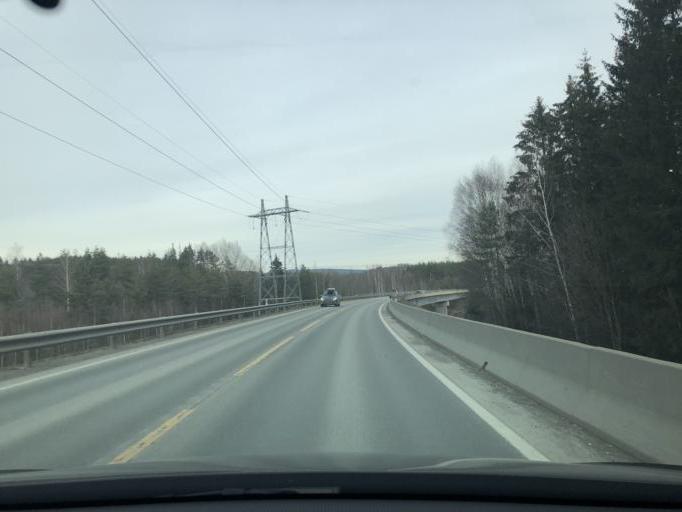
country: NO
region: Buskerud
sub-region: Ringerike
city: Honefoss
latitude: 60.1930
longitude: 10.2347
